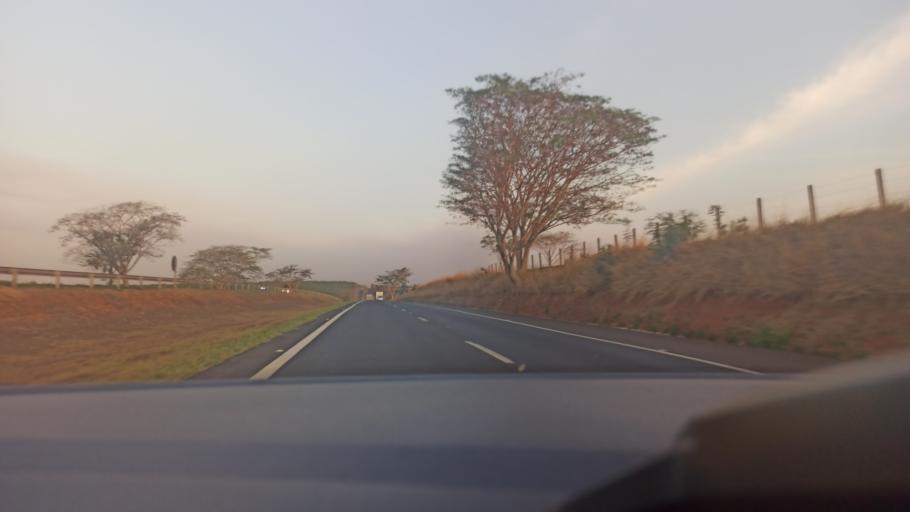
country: BR
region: Sao Paulo
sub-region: Taquaritinga
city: Taquaritinga
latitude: -21.4432
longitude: -48.6457
